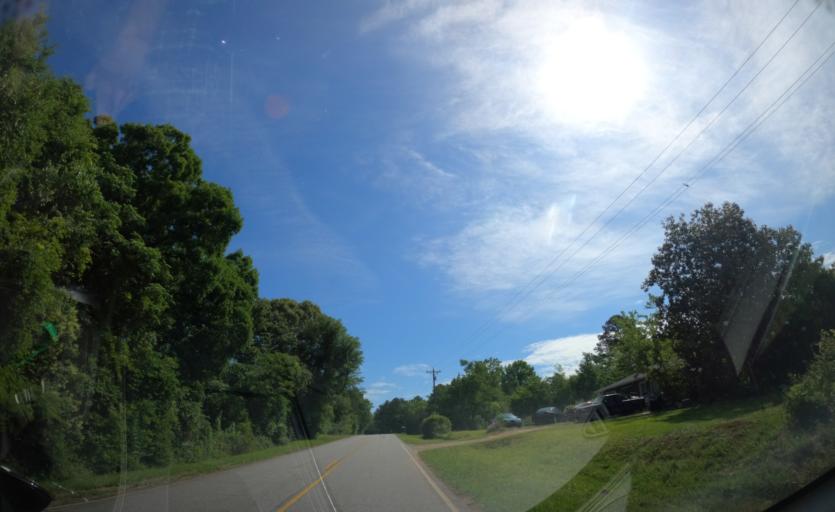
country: US
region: Georgia
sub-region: Elbert County
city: Elberton
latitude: 34.0810
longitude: -82.7340
